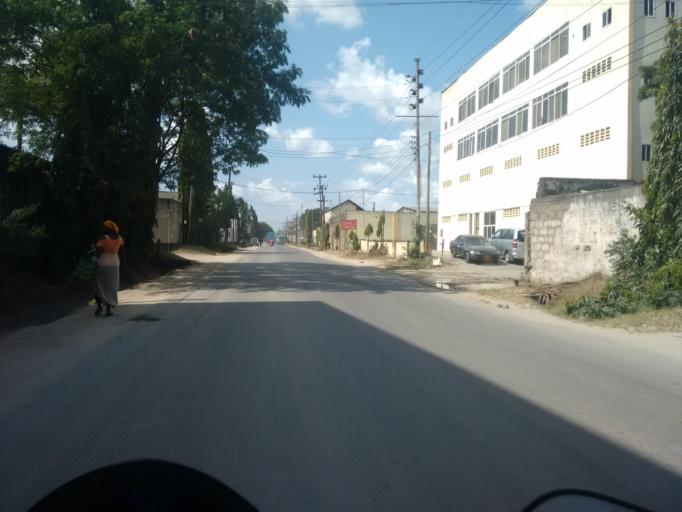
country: TZ
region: Dar es Salaam
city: Dar es Salaam
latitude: -6.8413
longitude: 39.2627
